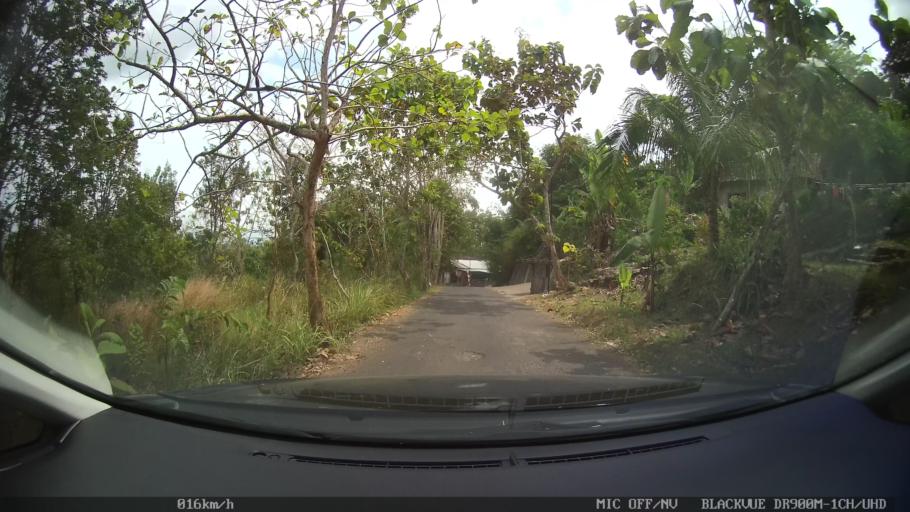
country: ID
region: Central Java
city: Candi Prambanan
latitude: -7.7954
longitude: 110.5204
